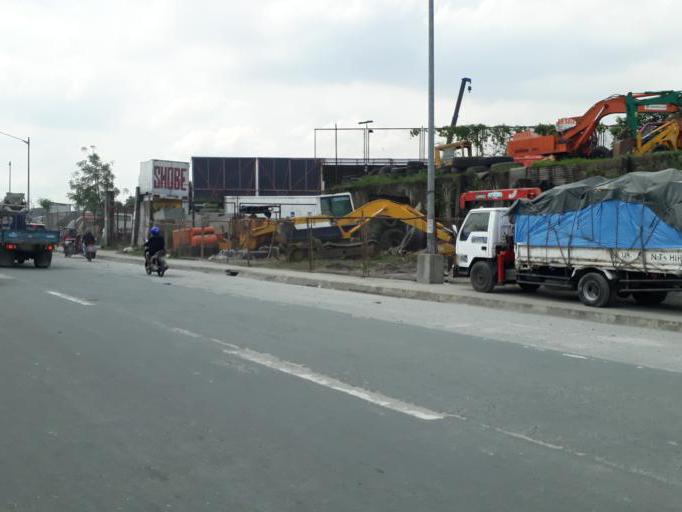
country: PH
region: Calabarzon
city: Bagong Pagasa
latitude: 14.6945
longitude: 121.0210
